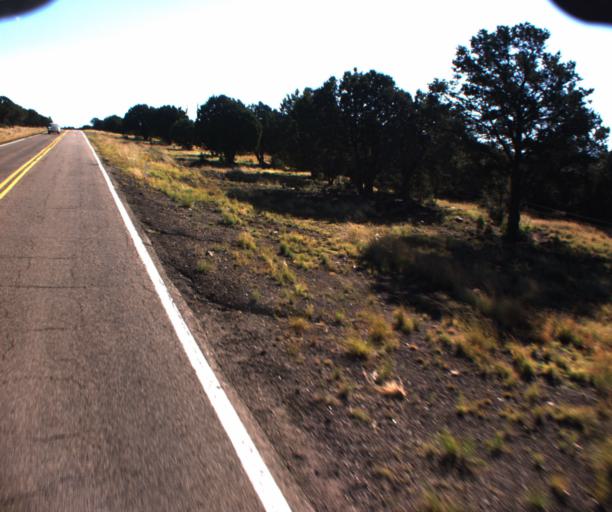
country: US
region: Arizona
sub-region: Navajo County
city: White Mountain Lake
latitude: 34.2897
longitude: -109.8153
